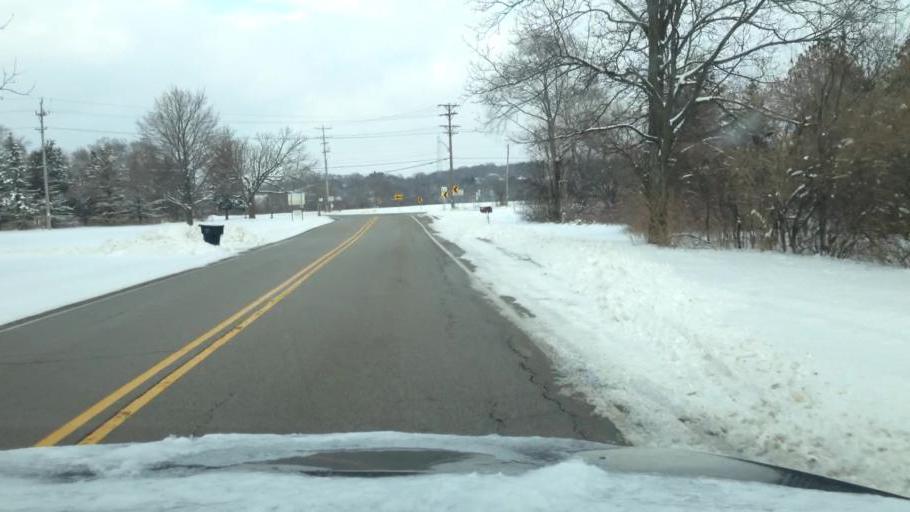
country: US
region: Wisconsin
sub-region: Waukesha County
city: North Prairie
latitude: 42.9066
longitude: -88.4093
